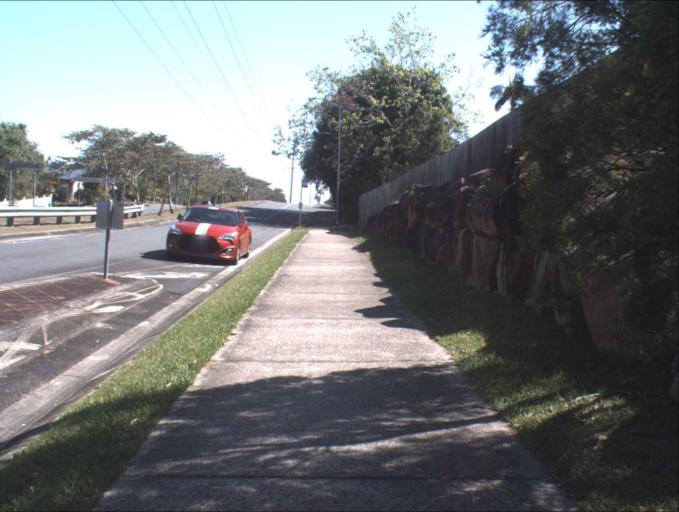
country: AU
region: Queensland
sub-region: Logan
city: Springwood
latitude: -27.6108
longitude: 153.1433
